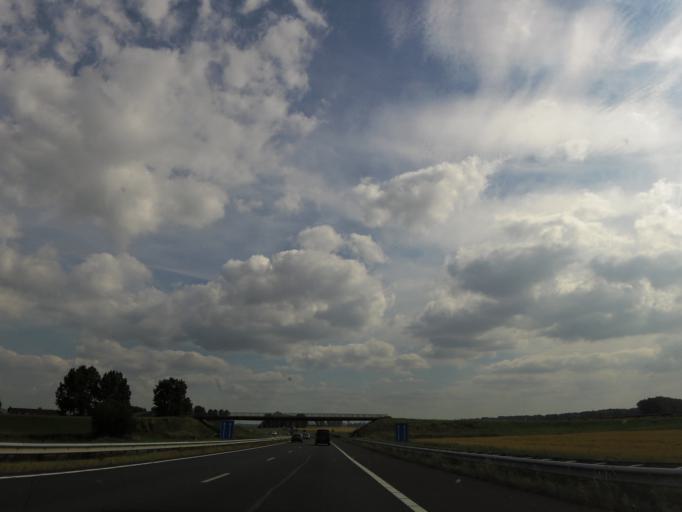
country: NL
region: North Brabant
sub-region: Gemeente Woensdrecht
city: Woensdrecht
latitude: 51.4268
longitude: 4.2762
